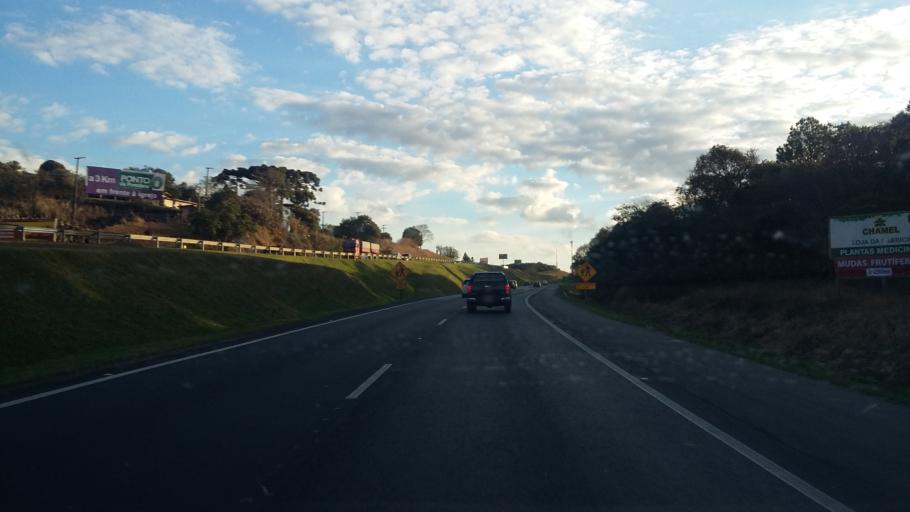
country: BR
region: Parana
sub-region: Campo Largo
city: Campo Largo
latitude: -25.4456
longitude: -49.4700
